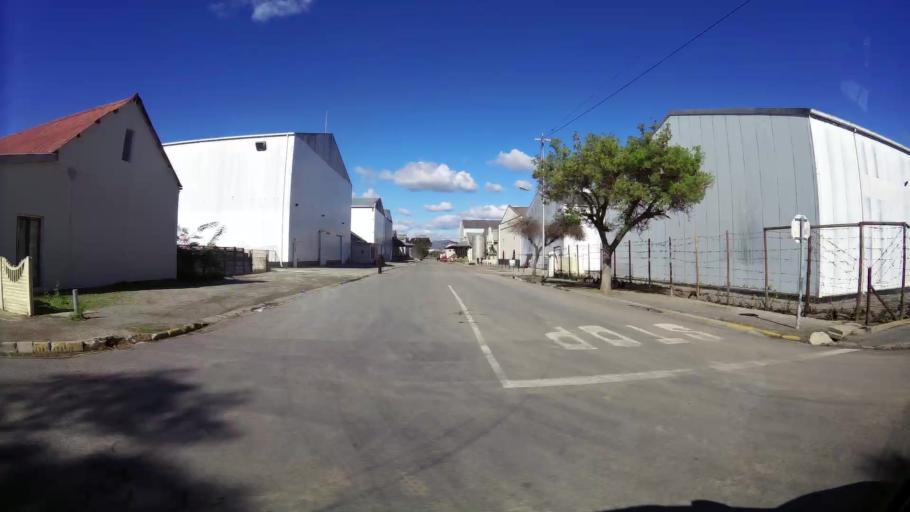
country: ZA
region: Western Cape
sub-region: Cape Winelands District Municipality
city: Ashton
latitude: -33.8084
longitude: 19.8800
